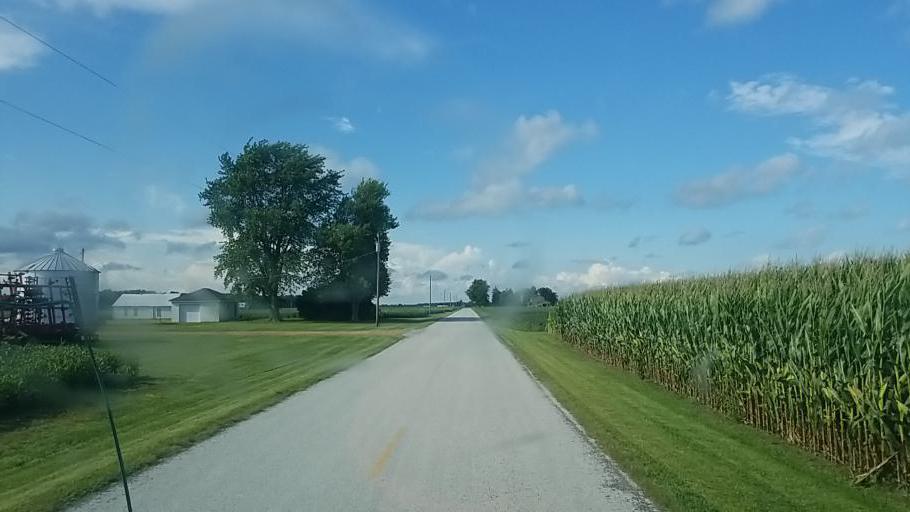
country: US
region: Ohio
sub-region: Hardin County
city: Forest
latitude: 40.7391
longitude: -83.5159
